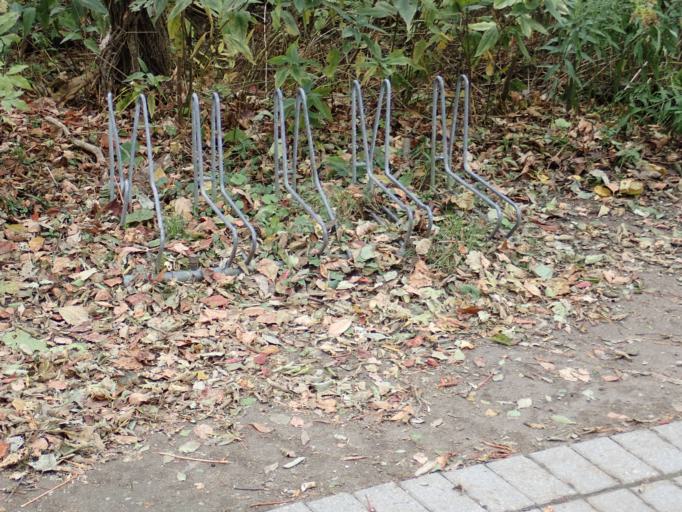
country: US
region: Ohio
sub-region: Erie County
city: Sandusky
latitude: 41.9141
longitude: -82.5096
